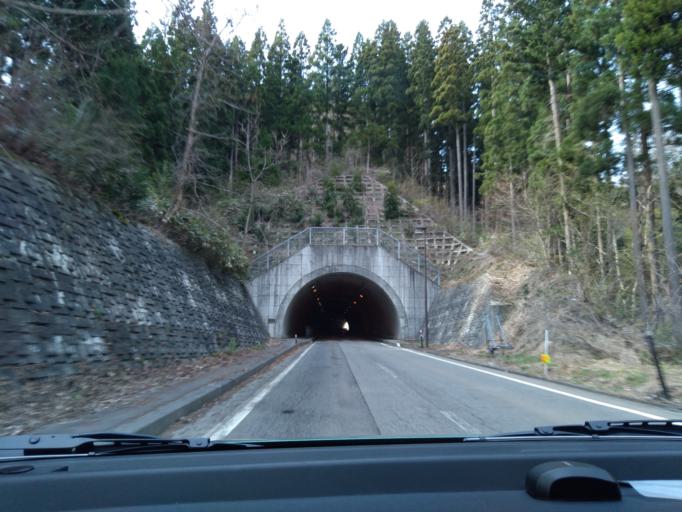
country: JP
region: Akita
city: Yokotemachi
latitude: 39.3115
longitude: 140.5843
